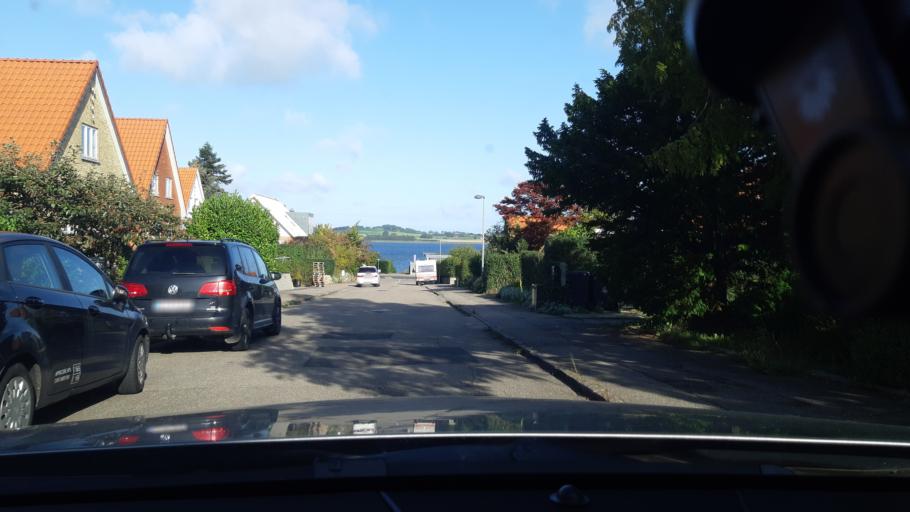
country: DK
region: Zealand
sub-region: Holbaek Kommune
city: Holbaek
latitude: 55.7163
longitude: 11.6852
